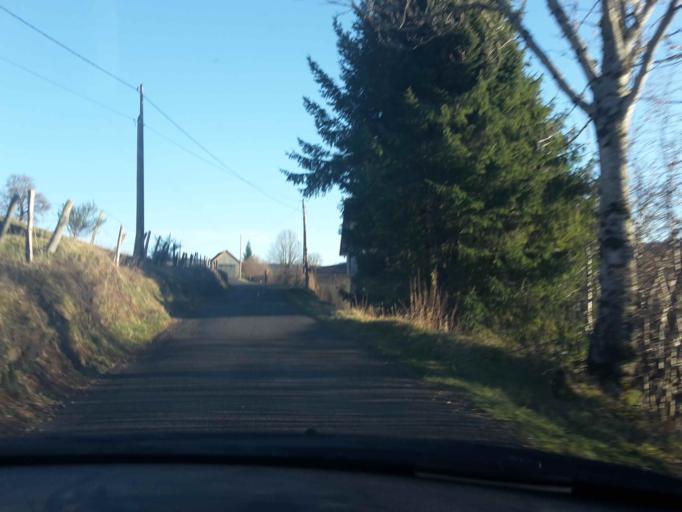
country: FR
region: Auvergne
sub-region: Departement du Cantal
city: Ydes
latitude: 45.2371
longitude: 2.5476
